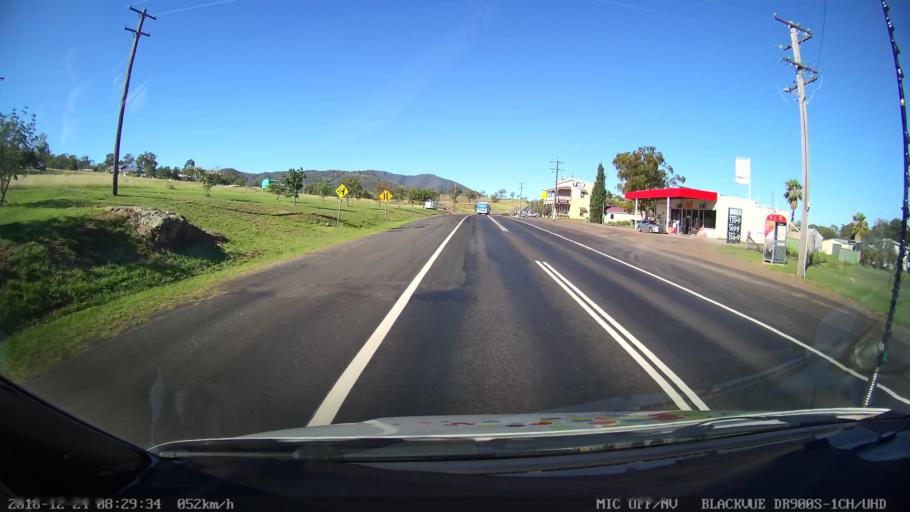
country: AU
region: New South Wales
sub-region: Tamworth Municipality
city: Phillip
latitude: -31.2636
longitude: 150.7330
